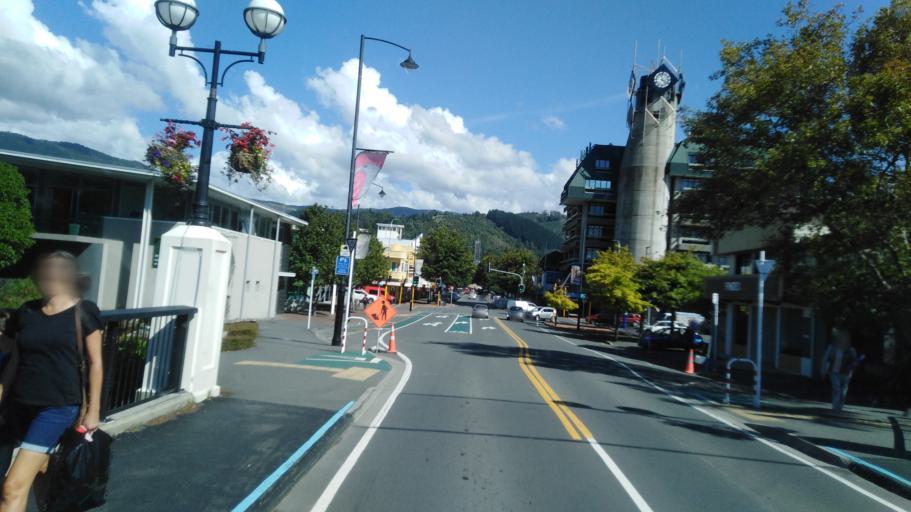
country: NZ
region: Nelson
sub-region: Nelson City
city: Nelson
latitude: -41.2700
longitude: 173.2841
